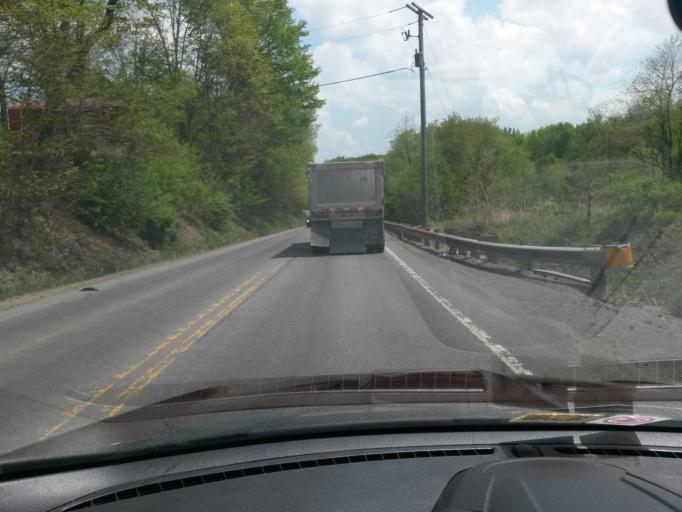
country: US
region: West Virginia
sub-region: Greenbrier County
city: Rainelle
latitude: 37.9701
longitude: -80.7052
